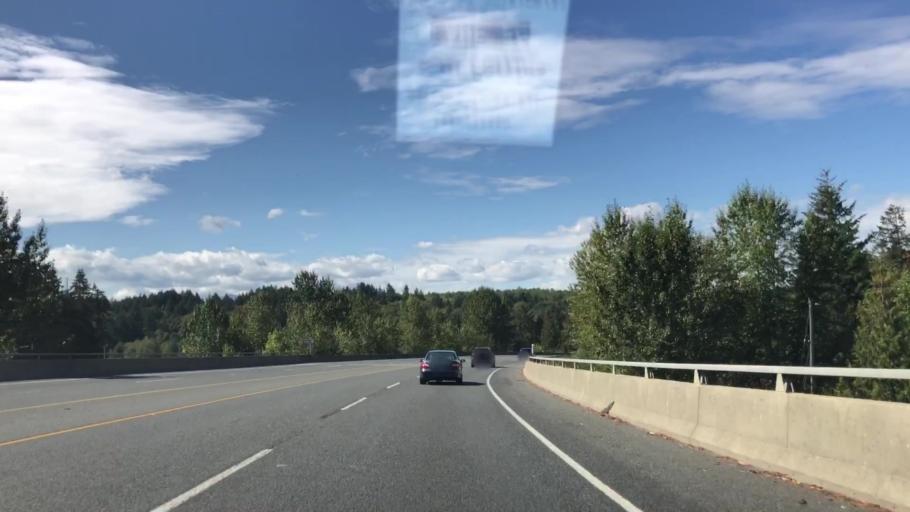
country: CA
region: British Columbia
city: Nanaimo
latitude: 49.1141
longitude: -123.8793
